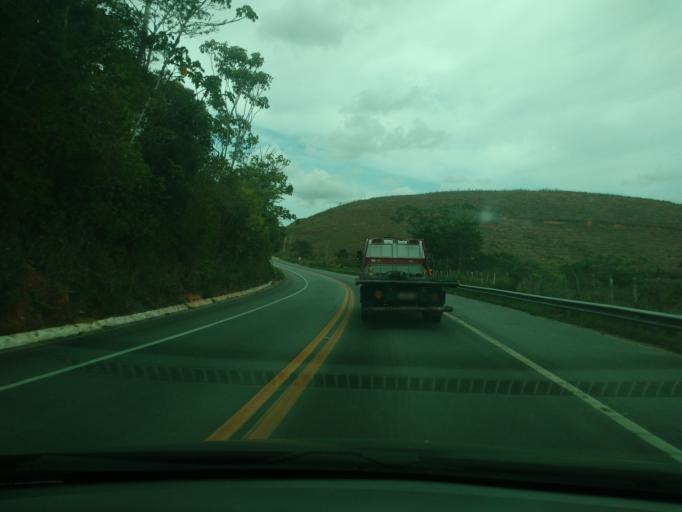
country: BR
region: Alagoas
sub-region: Murici
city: Murici
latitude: -9.3318
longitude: -35.9141
